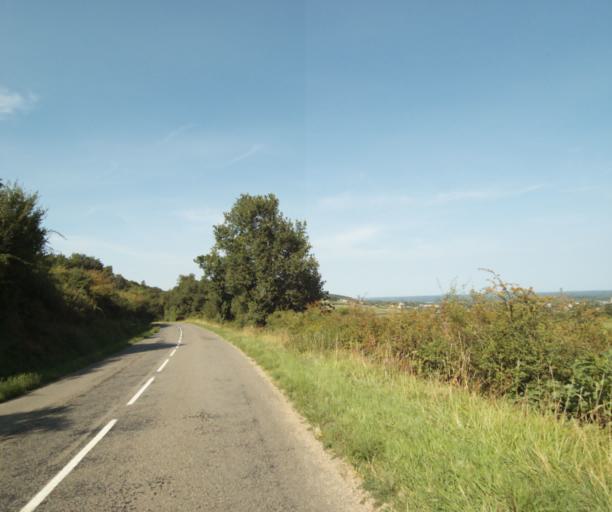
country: FR
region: Bourgogne
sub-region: Departement de Saone-et-Loire
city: Tournus
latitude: 46.5543
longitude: 4.8765
